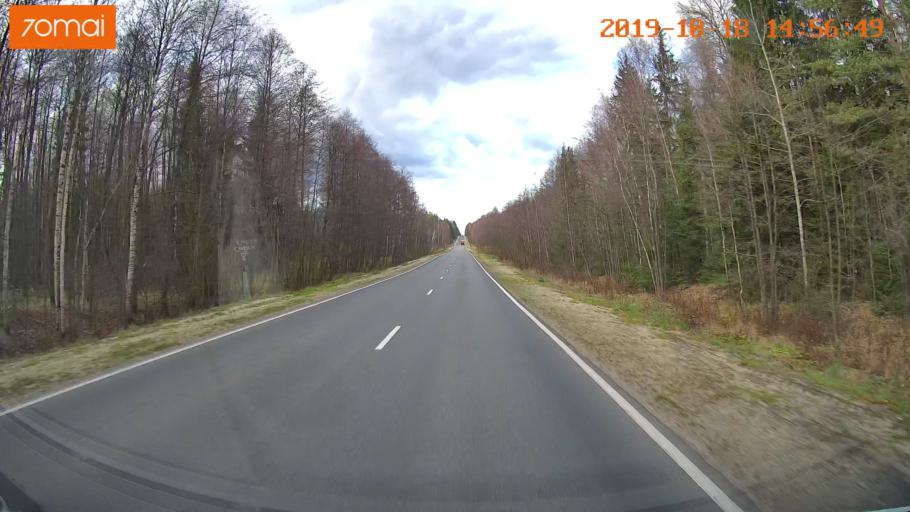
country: RU
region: Vladimir
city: Kurlovo
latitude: 55.4703
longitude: 40.5852
